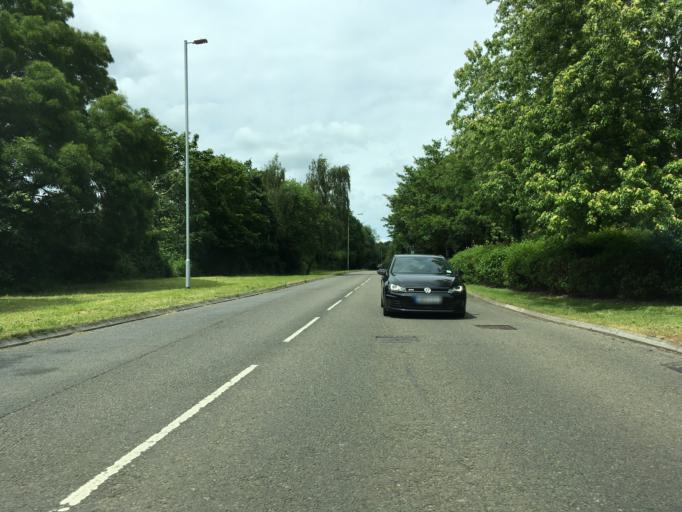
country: GB
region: England
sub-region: Wiltshire
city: Lydiard Tregoze
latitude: 51.5594
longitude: -1.8339
